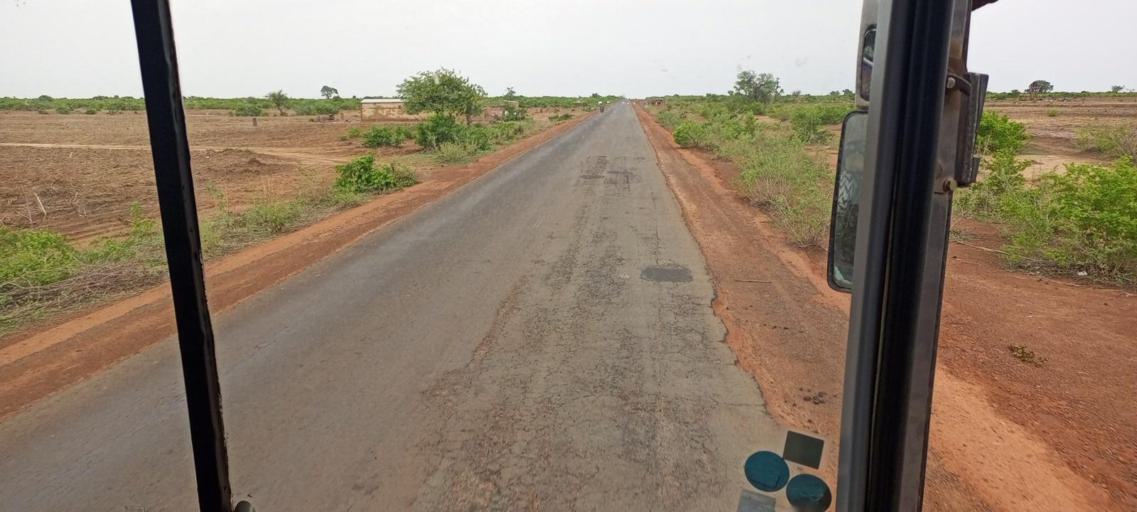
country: ML
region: Segou
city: Bla
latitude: 12.7073
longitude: -5.7243
